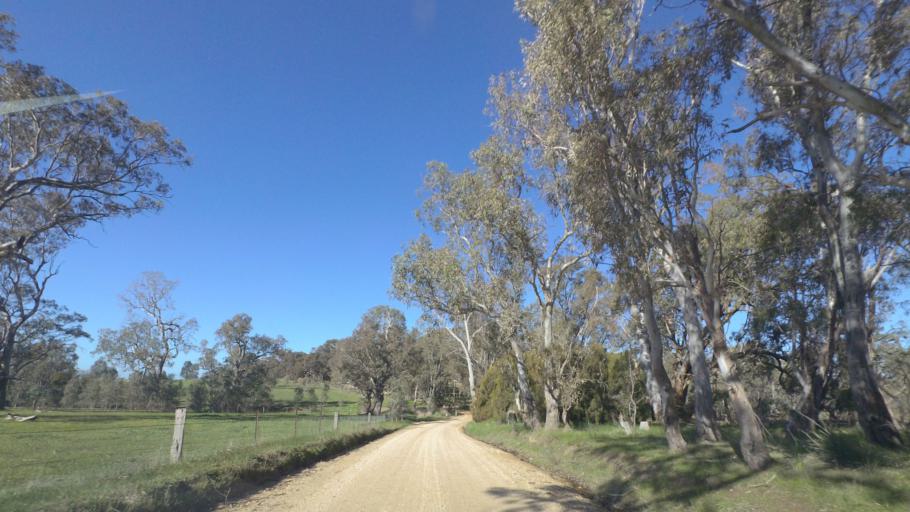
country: AU
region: Victoria
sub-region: Mount Alexander
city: Castlemaine
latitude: -36.9668
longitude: 144.3457
